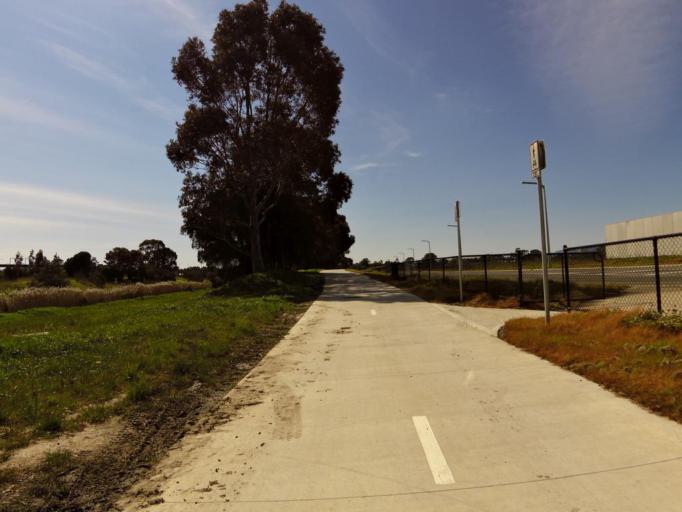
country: AU
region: Victoria
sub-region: Greater Dandenong
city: Keysborough
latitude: -38.0082
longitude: 145.1916
